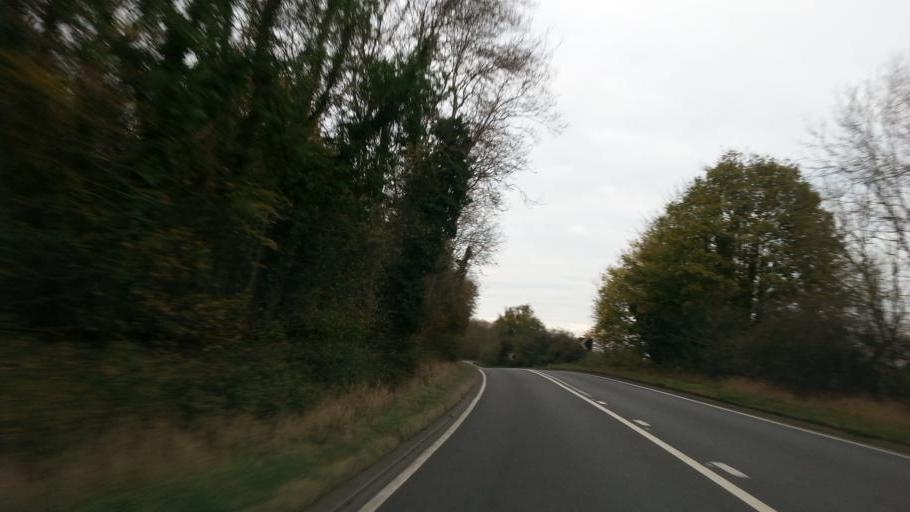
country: GB
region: England
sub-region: Northamptonshire
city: Corby
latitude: 52.5027
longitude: -0.6220
